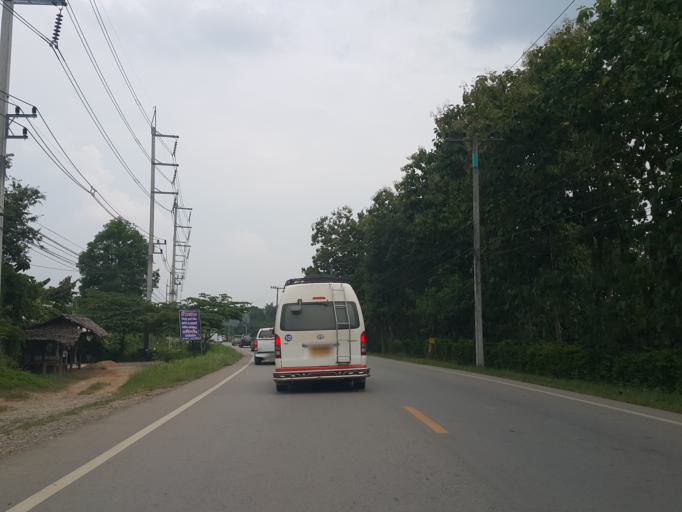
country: TH
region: Chiang Mai
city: Mae Taeng
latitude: 19.0914
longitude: 98.8861
